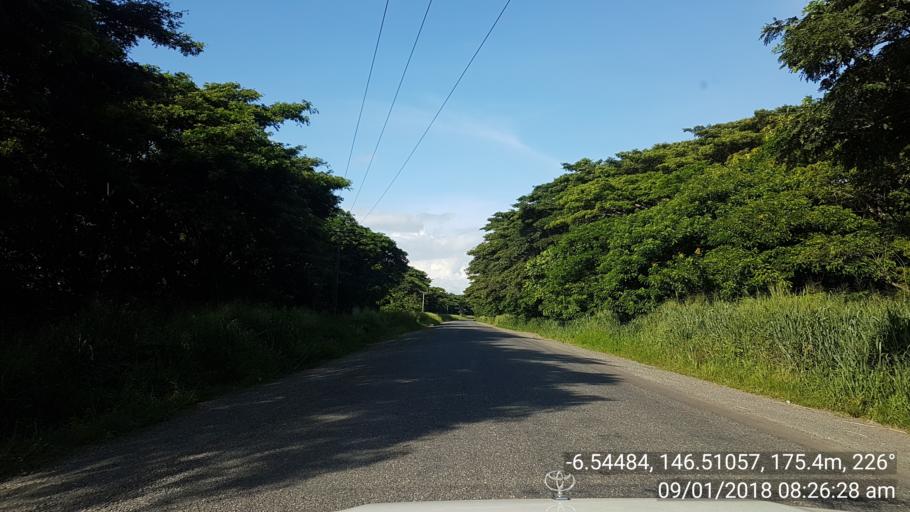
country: PG
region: Morobe
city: Lae
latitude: -6.5447
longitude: 146.5105
